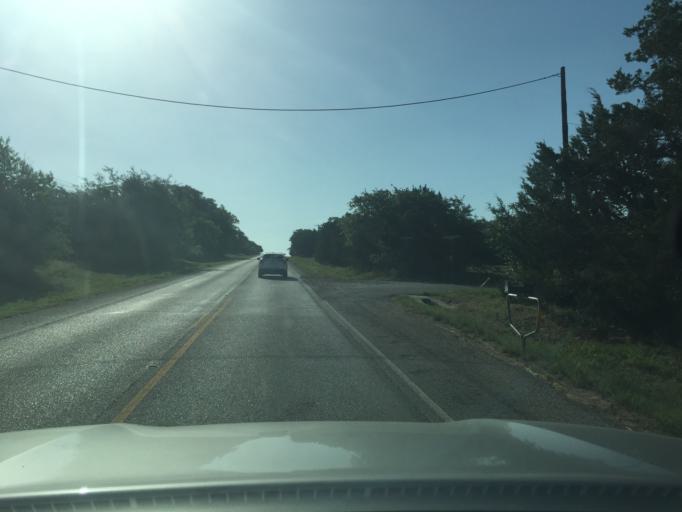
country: US
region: Texas
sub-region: Blanco County
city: Blanco
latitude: 30.1113
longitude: -98.3318
